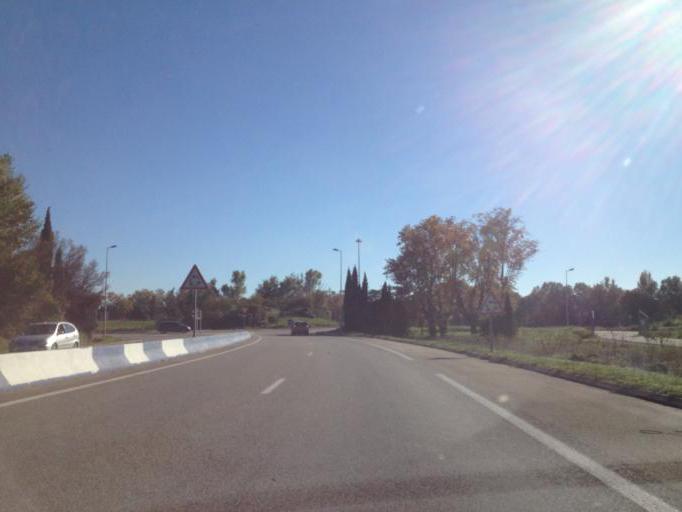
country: FR
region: Provence-Alpes-Cote d'Azur
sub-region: Departement du Vaucluse
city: Sorgues
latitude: 44.0007
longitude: 4.8648
